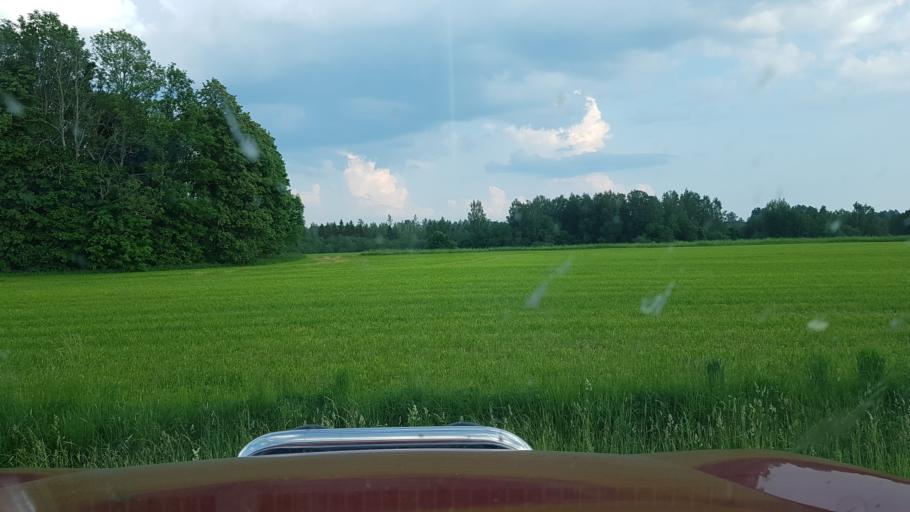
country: EE
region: Tartu
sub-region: UElenurme vald
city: Ulenurme
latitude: 58.0891
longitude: 26.8152
